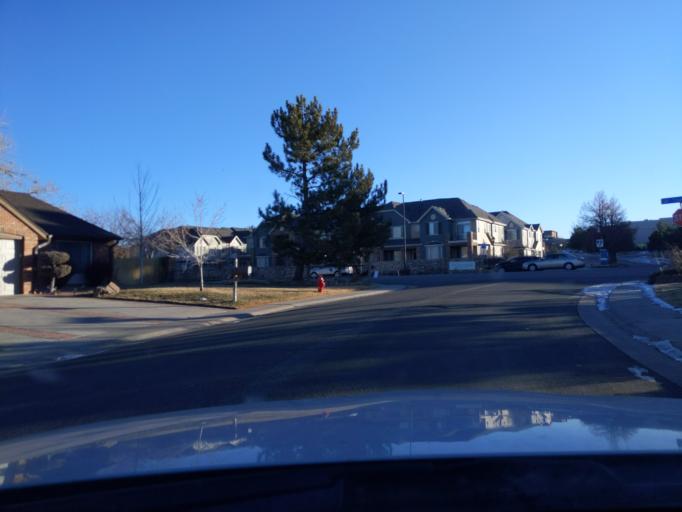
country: US
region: Colorado
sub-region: Arapahoe County
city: Centennial
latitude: 39.5679
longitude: -104.8862
